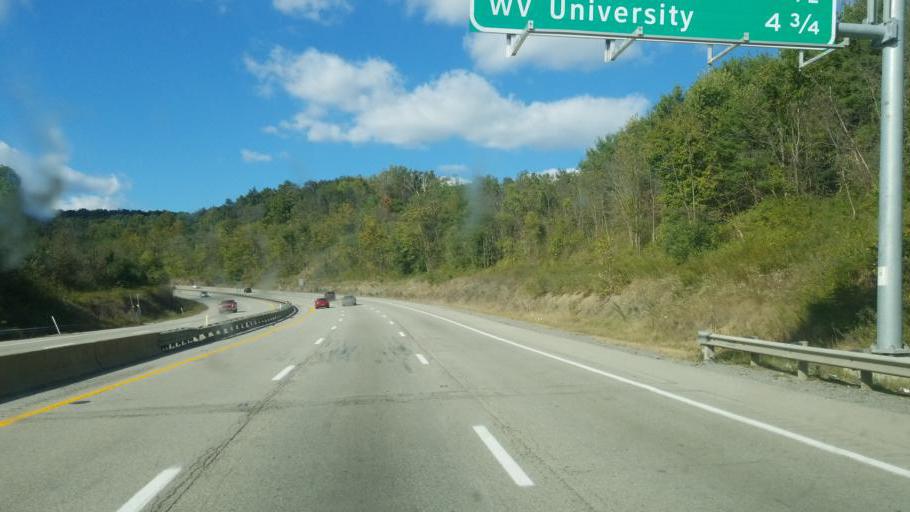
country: US
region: West Virginia
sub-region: Monongalia County
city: Westover
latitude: 39.5904
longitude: -79.9793
